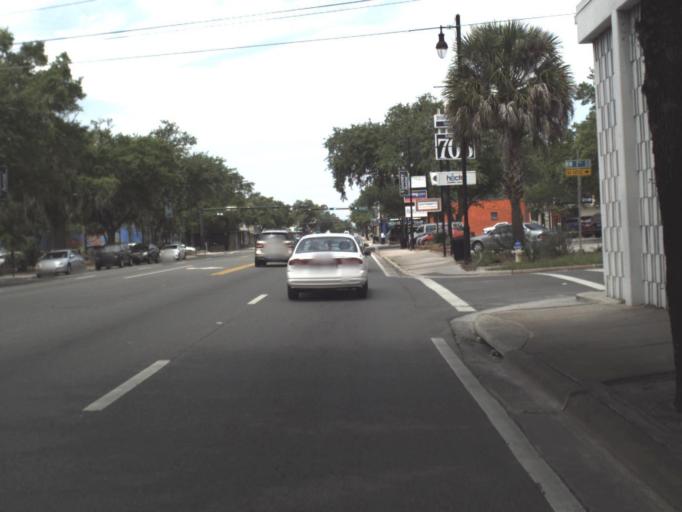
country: US
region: Florida
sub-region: Alachua County
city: Gainesville
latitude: 29.6521
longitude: -82.3314
